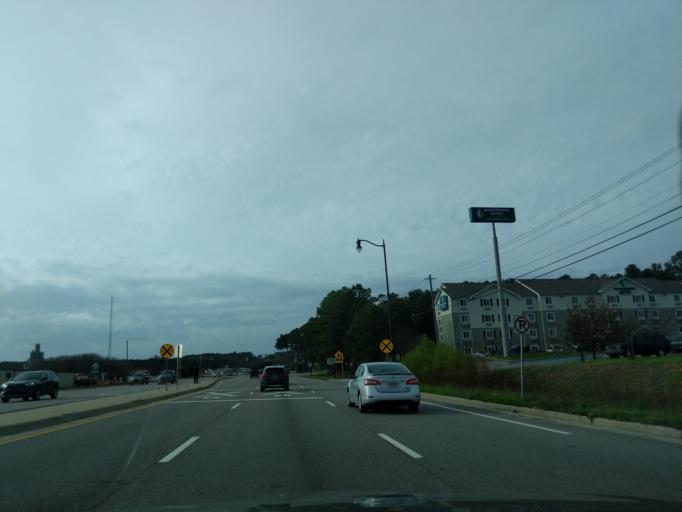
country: US
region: Georgia
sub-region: Columbia County
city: Martinez
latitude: 33.5235
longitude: -82.0353
